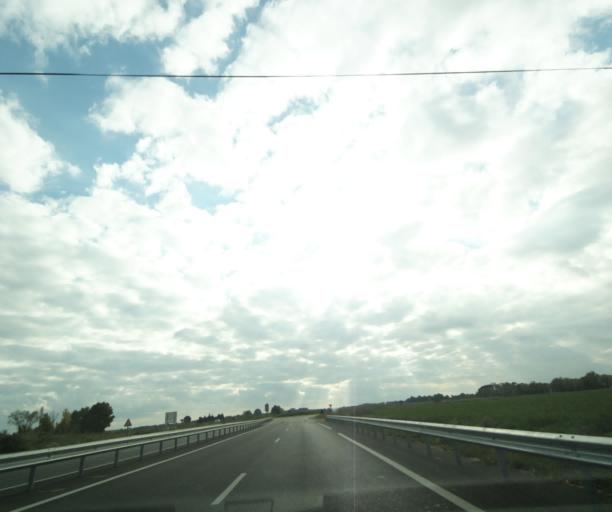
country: FR
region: Languedoc-Roussillon
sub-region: Departement du Gard
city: Aimargues
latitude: 43.6590
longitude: 4.2046
